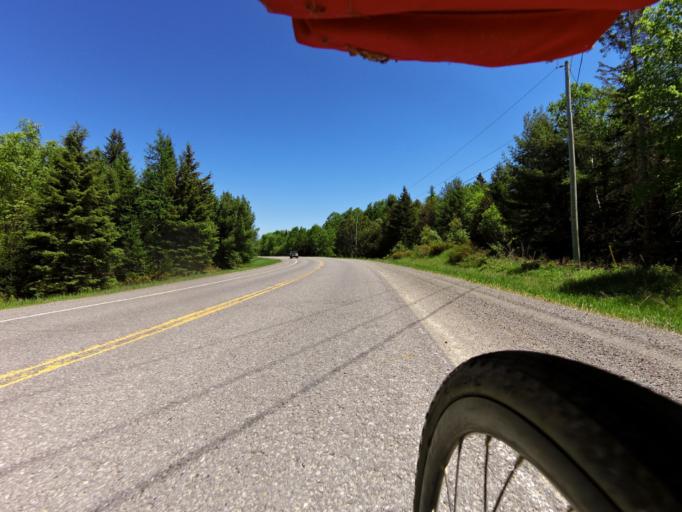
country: CA
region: Ontario
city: Carleton Place
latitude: 45.1831
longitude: -76.3862
